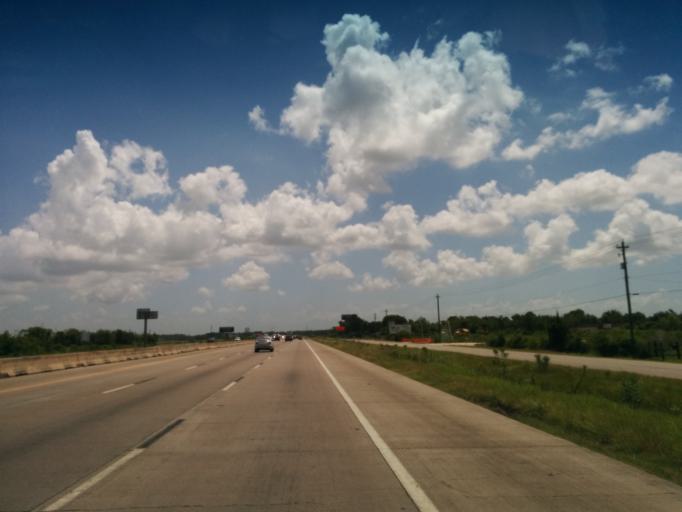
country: US
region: Texas
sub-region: Chambers County
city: Mont Belvieu
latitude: 29.8096
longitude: -94.9532
